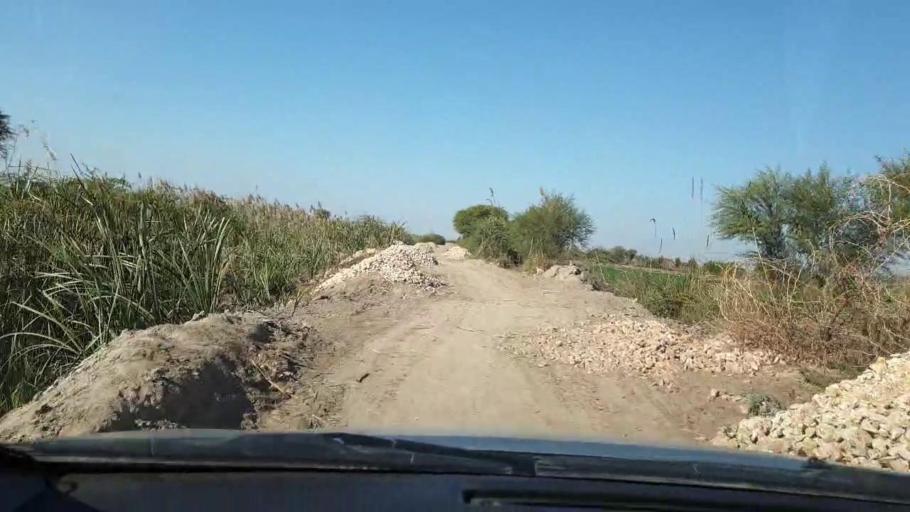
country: PK
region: Sindh
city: Berani
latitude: 25.7324
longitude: 68.9841
